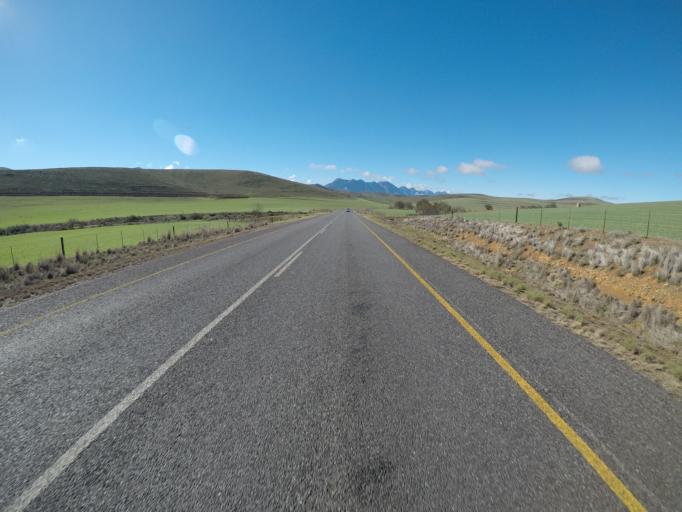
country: ZA
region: Western Cape
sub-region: Overberg District Municipality
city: Caledon
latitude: -34.0948
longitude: 19.5411
